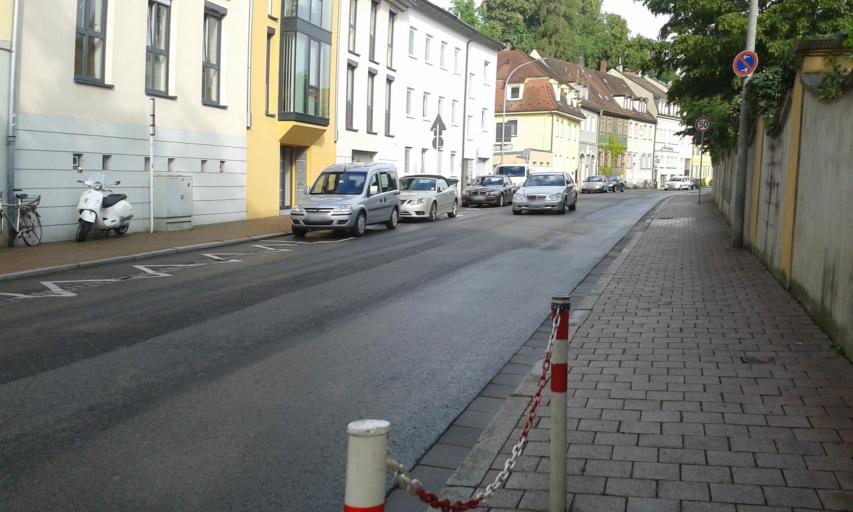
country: DE
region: Bavaria
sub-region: Upper Franconia
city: Bamberg
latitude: 49.8942
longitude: 10.8805
